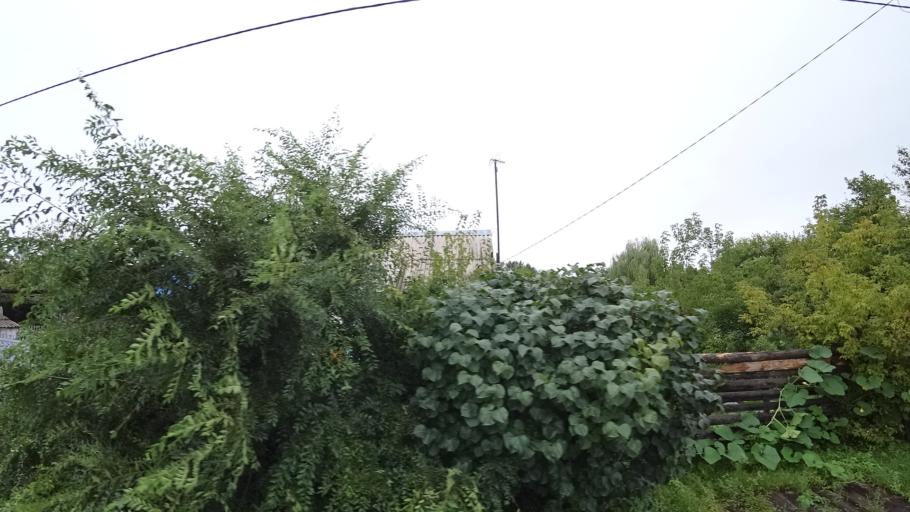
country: RU
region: Primorskiy
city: Monastyrishche
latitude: 44.2045
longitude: 132.4233
